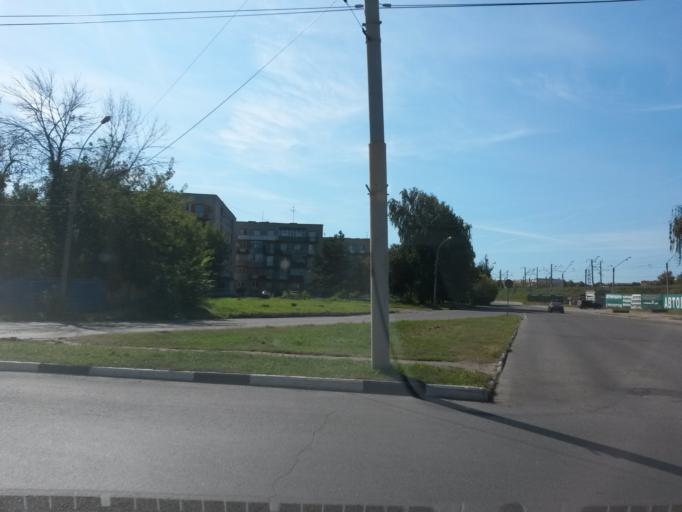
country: RU
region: Jaroslavl
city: Yaroslavl
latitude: 57.6448
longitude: 39.8813
